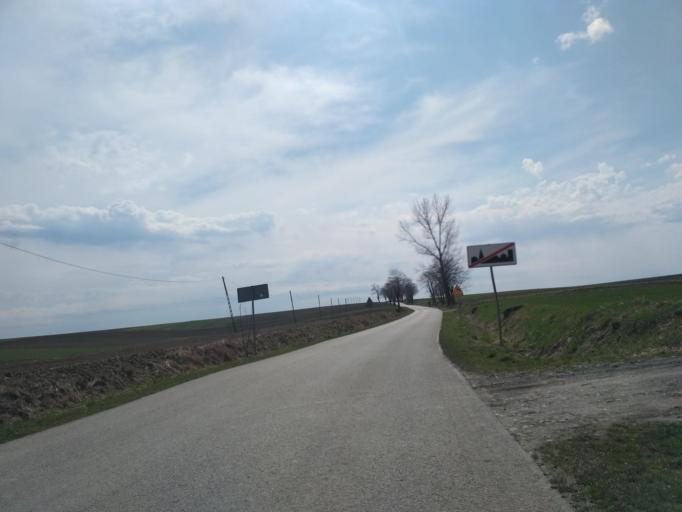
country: PL
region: Subcarpathian Voivodeship
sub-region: Powiat ropczycko-sedziszowski
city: Iwierzyce
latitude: 50.0198
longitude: 21.7688
